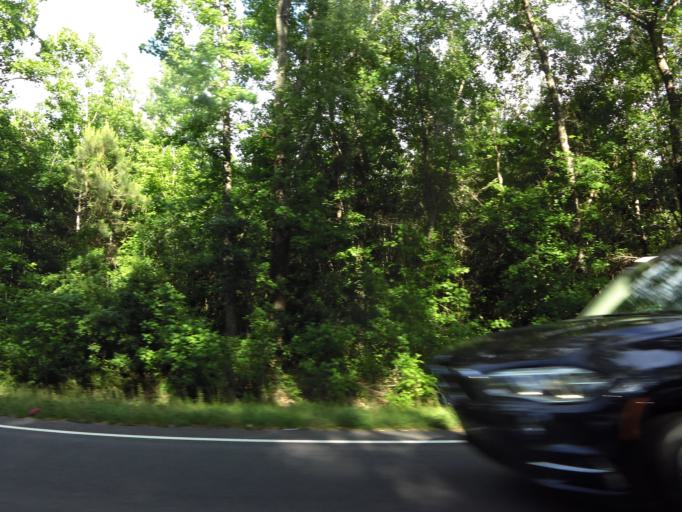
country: US
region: South Carolina
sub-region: Allendale County
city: Fairfax
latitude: 32.9457
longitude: -81.2365
